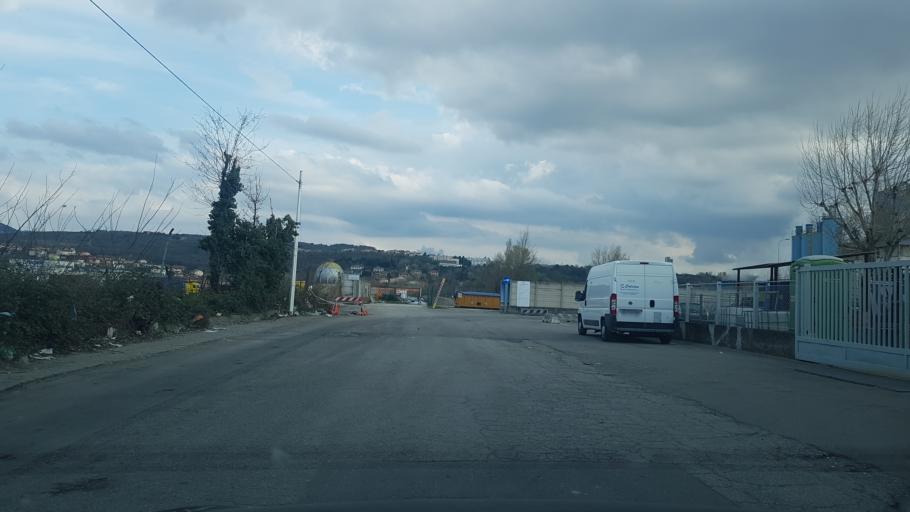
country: IT
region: Friuli Venezia Giulia
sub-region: Provincia di Trieste
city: Domio
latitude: 45.6124
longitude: 13.8004
